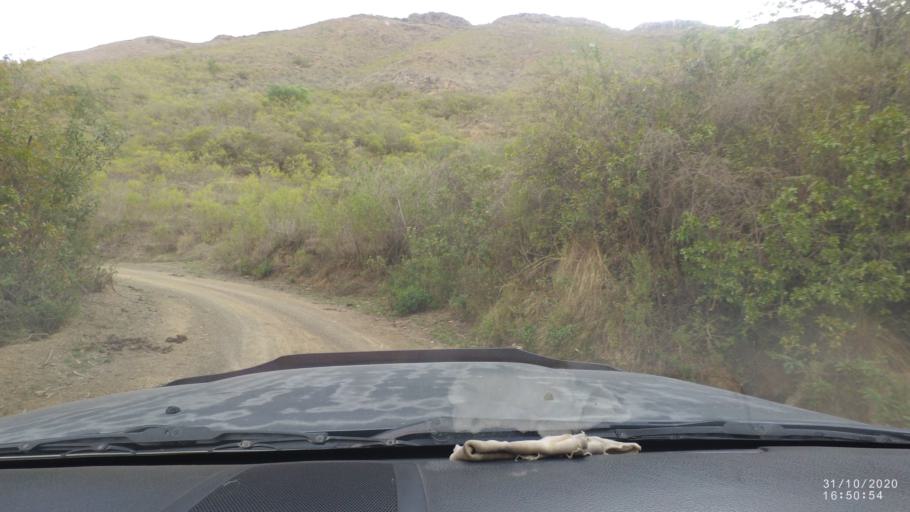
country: BO
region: Chuquisaca
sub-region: Provincia Zudanez
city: Mojocoya
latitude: -18.5103
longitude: -64.5724
